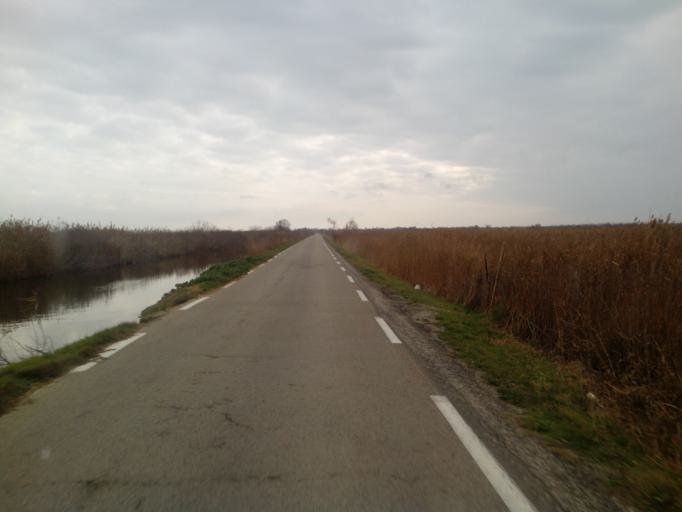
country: FR
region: Languedoc-Roussillon
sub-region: Departement du Gard
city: Vauvert
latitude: 43.6173
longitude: 4.3227
